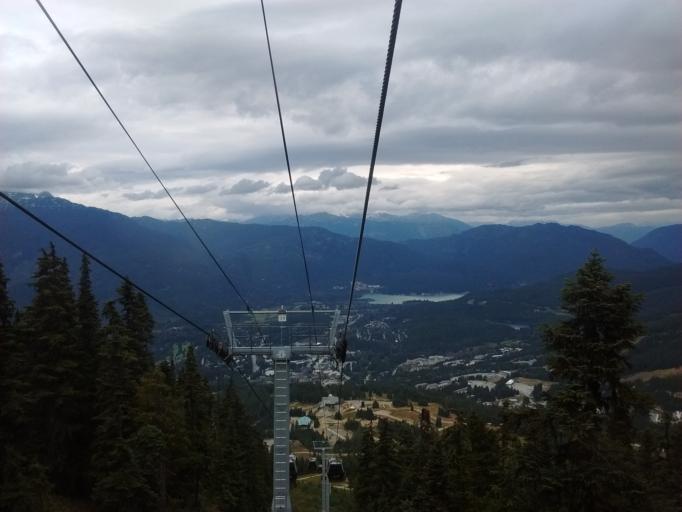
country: CA
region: British Columbia
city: Whistler
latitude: 50.0884
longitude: -122.9499
